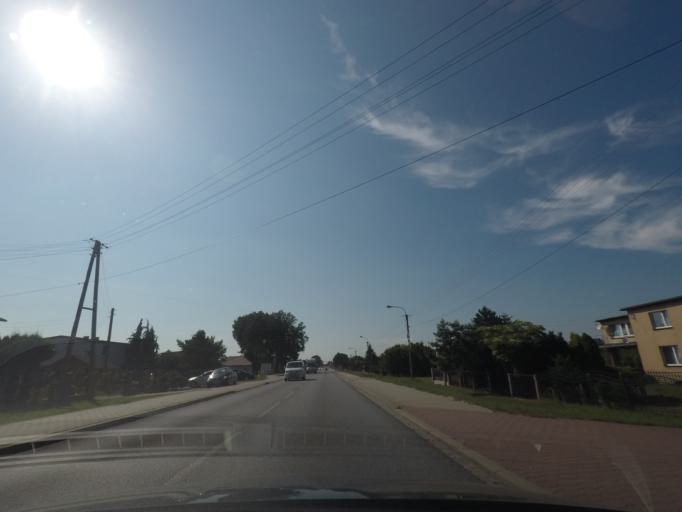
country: PL
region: Silesian Voivodeship
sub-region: Powiat pszczynski
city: Suszec
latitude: 50.0297
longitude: 18.7901
